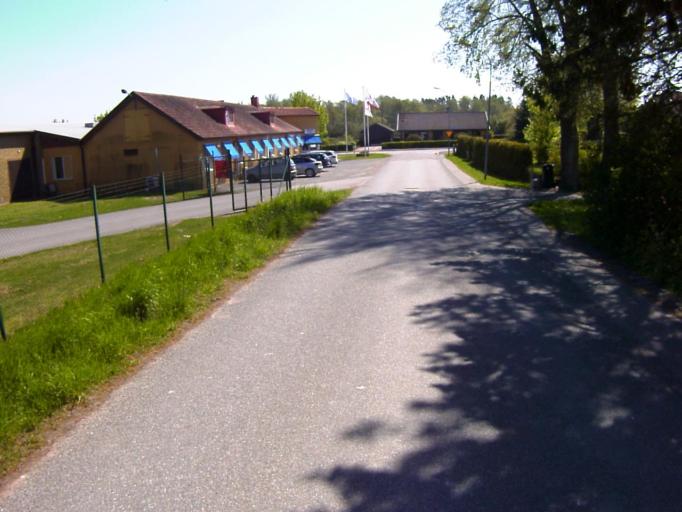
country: SE
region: Skane
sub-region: Kristianstads Kommun
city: Degeberga
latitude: 55.8993
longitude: 14.0964
